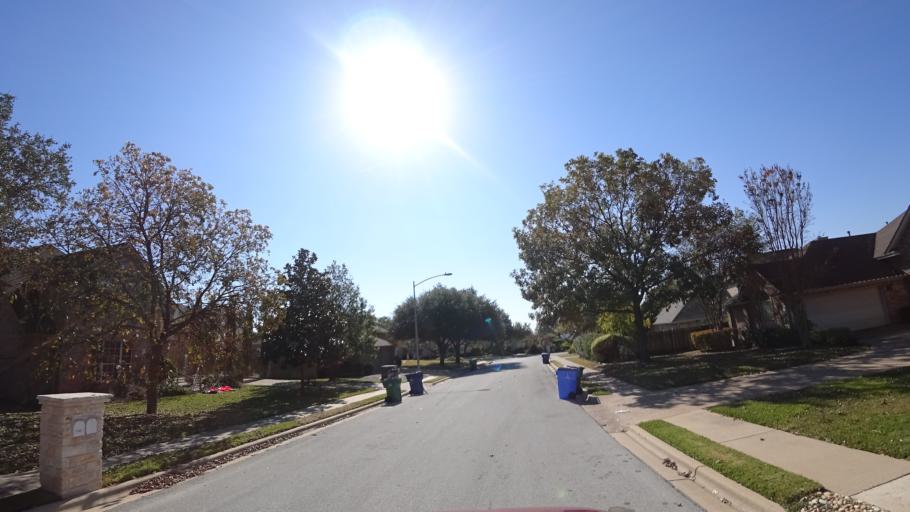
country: US
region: Texas
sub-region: Travis County
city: Lost Creek
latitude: 30.3733
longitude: -97.8466
